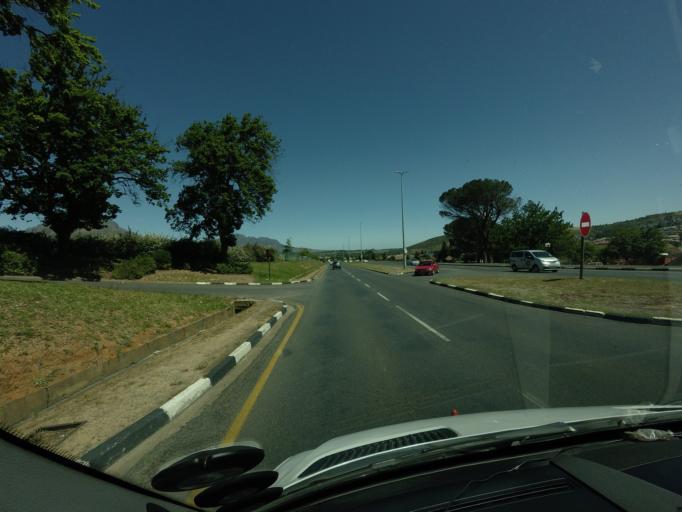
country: ZA
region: Western Cape
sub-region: Cape Winelands District Municipality
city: Stellenbosch
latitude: -33.9153
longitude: 18.8588
